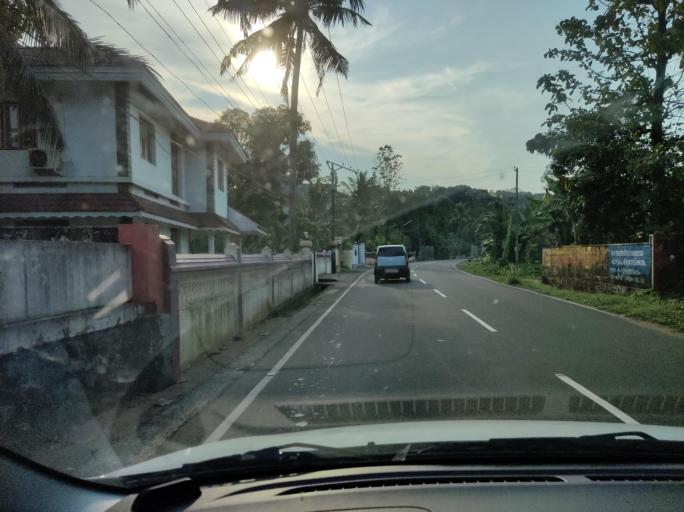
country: IN
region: Kerala
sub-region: Kottayam
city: Kottayam
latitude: 9.6462
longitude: 76.5256
